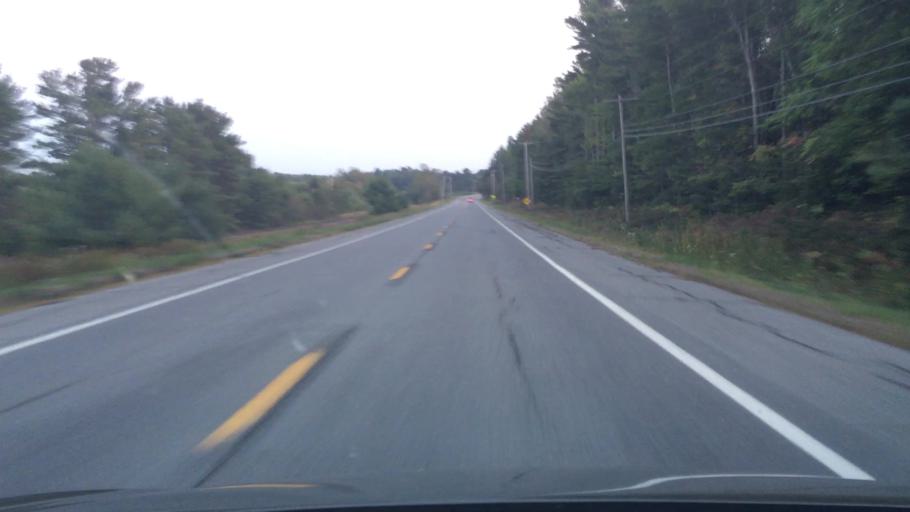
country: US
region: Maine
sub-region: Waldo County
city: Stockton Springs
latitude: 44.5431
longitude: -68.8631
